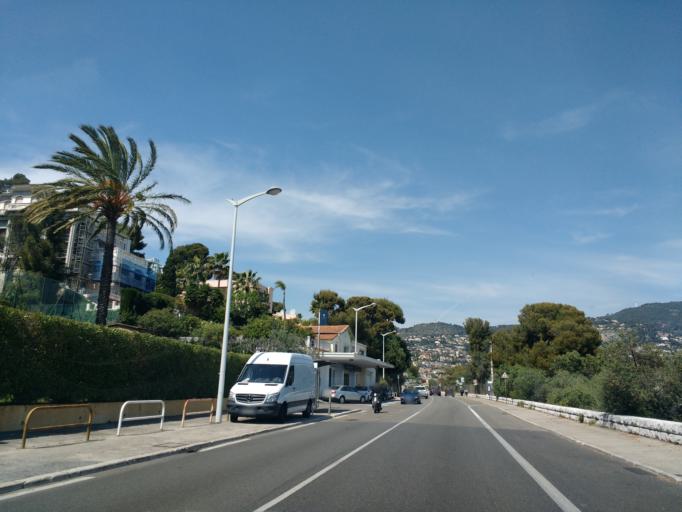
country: FR
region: Provence-Alpes-Cote d'Azur
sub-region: Departement des Alpes-Maritimes
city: Villefranche-sur-Mer
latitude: 43.6913
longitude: 7.3070
